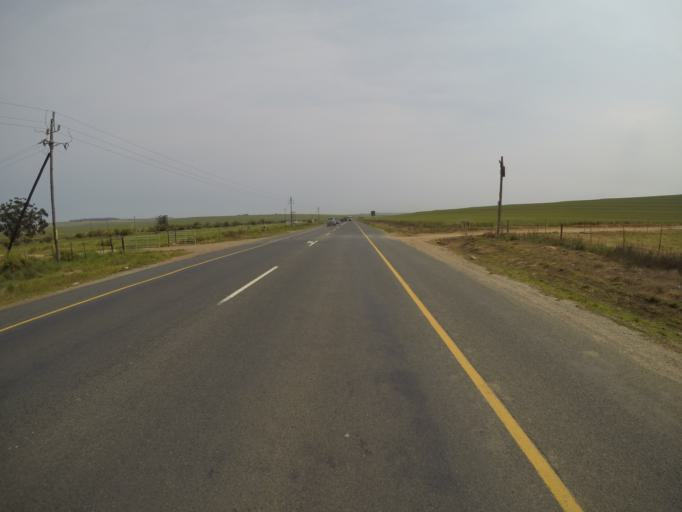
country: ZA
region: Western Cape
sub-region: West Coast District Municipality
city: Malmesbury
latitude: -33.4767
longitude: 18.8020
